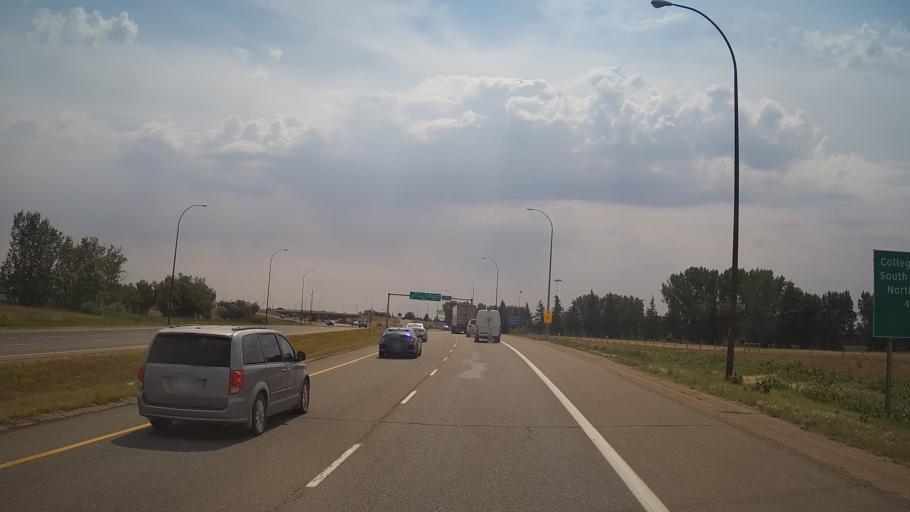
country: CA
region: Alberta
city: Medicine Hat
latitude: 50.0160
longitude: -110.6897
